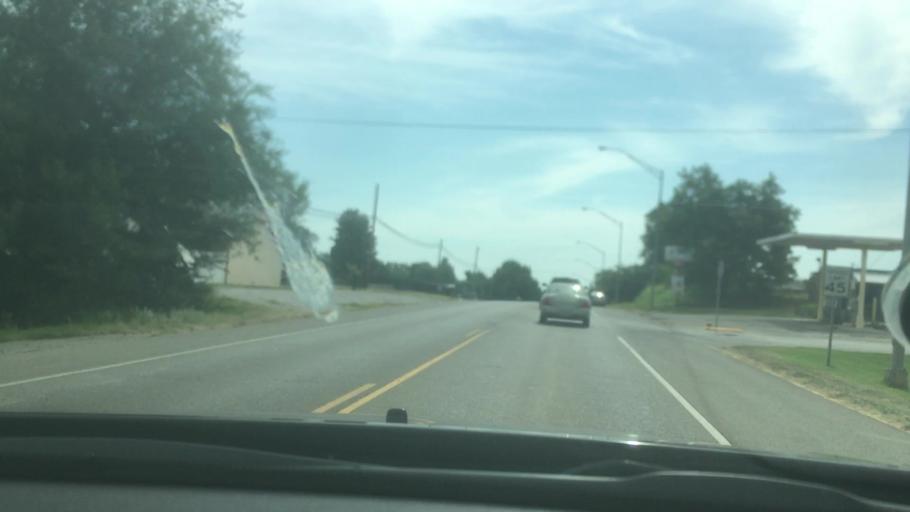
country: US
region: Oklahoma
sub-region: Garvin County
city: Maysville
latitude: 34.8173
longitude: -97.4209
